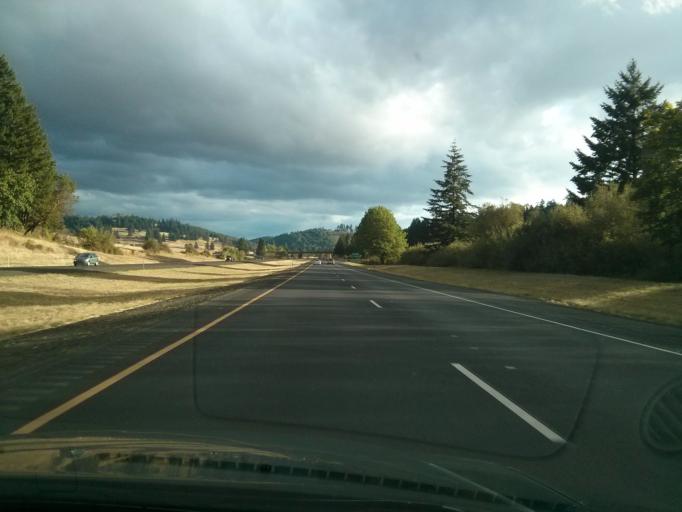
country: US
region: Oregon
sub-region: Douglas County
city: Yoncalla
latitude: 43.5195
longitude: -123.3135
